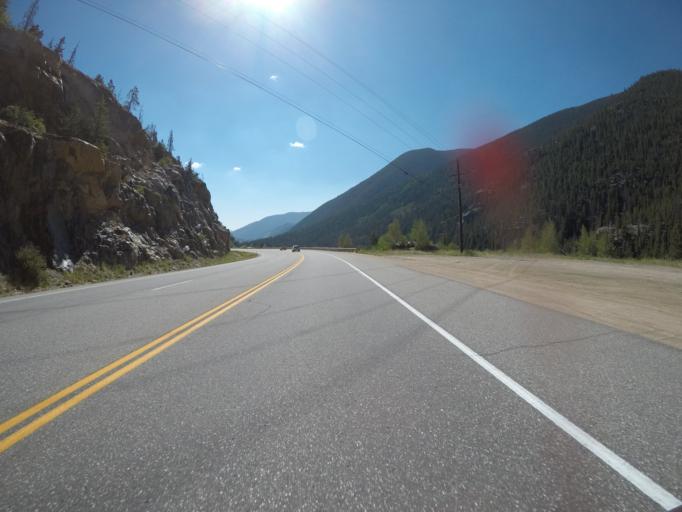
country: US
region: Colorado
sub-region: Clear Creek County
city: Georgetown
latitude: 39.7640
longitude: -105.7412
